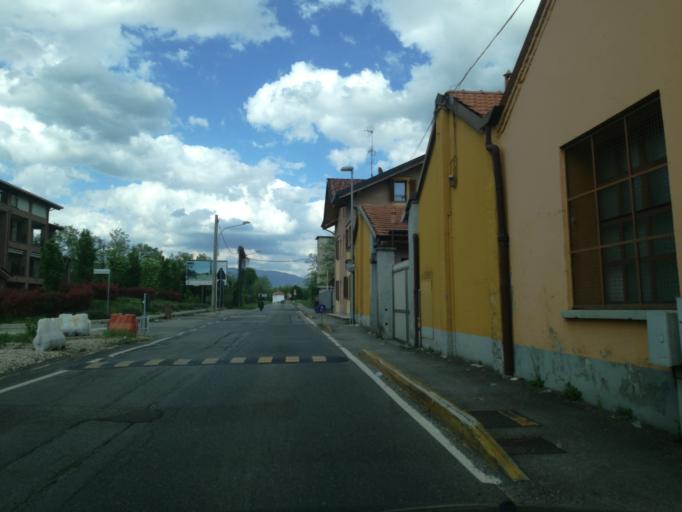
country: IT
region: Lombardy
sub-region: Provincia di Monza e Brianza
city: Ronco Briantino
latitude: 45.6599
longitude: 9.3913
